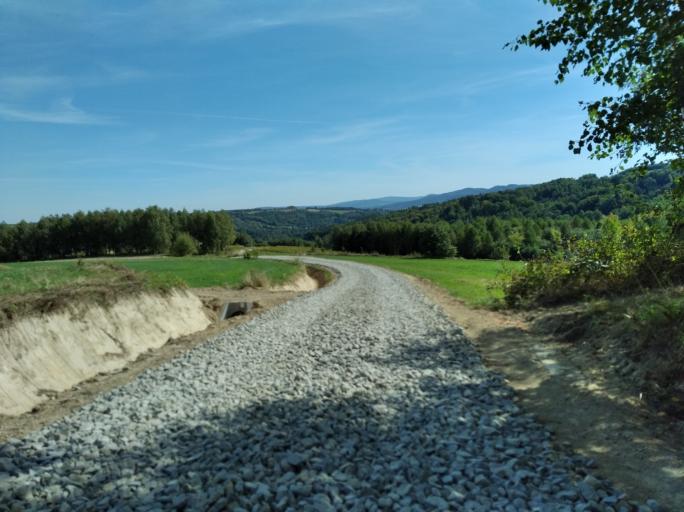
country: PL
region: Subcarpathian Voivodeship
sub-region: Powiat strzyzowski
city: Wisniowa
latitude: 49.9003
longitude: 21.6242
